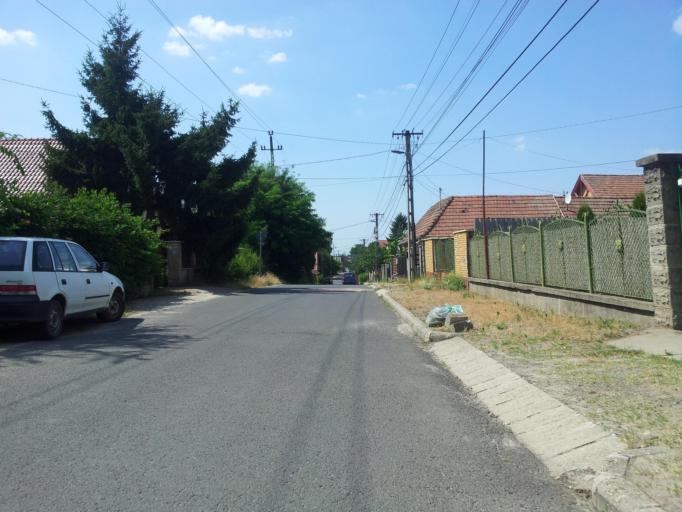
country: HU
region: Pest
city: Veresegyhaz
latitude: 47.6486
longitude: 19.2982
